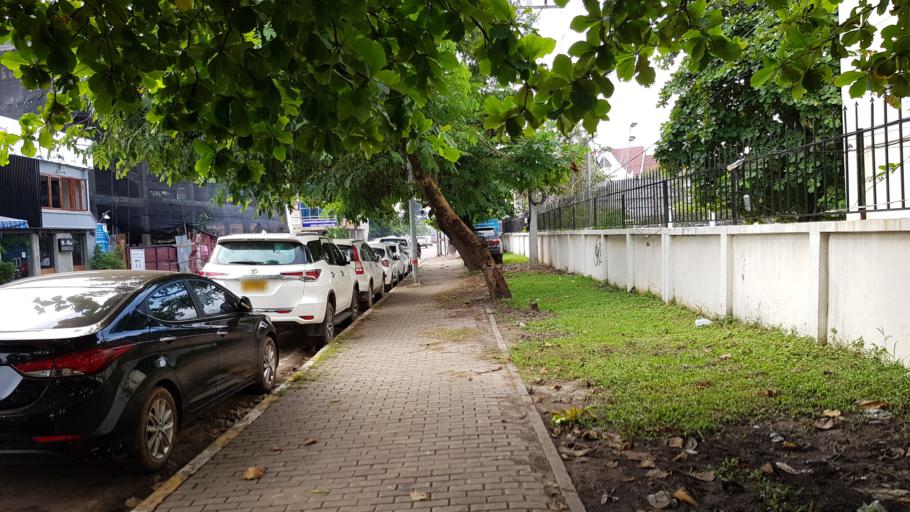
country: LA
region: Vientiane
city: Vientiane
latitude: 17.9683
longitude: 102.5990
